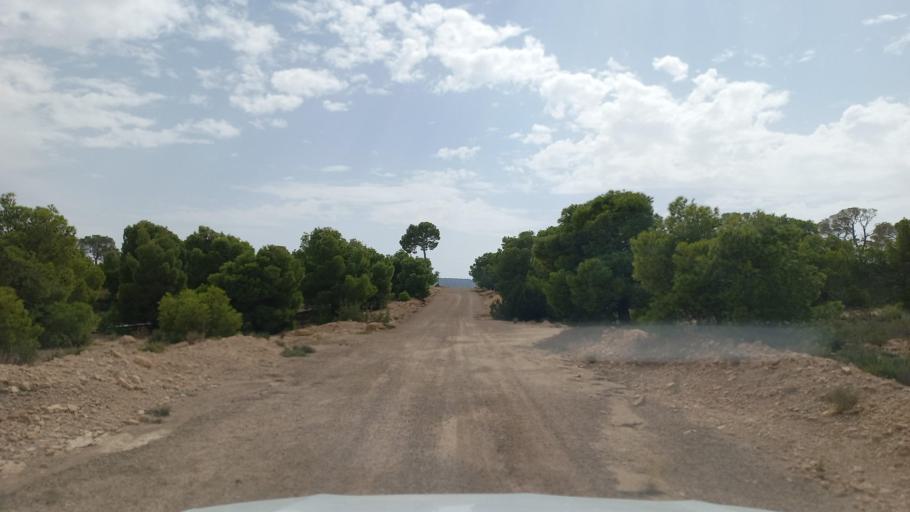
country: TN
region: Al Qasrayn
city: Kasserine
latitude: 35.3805
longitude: 8.8807
